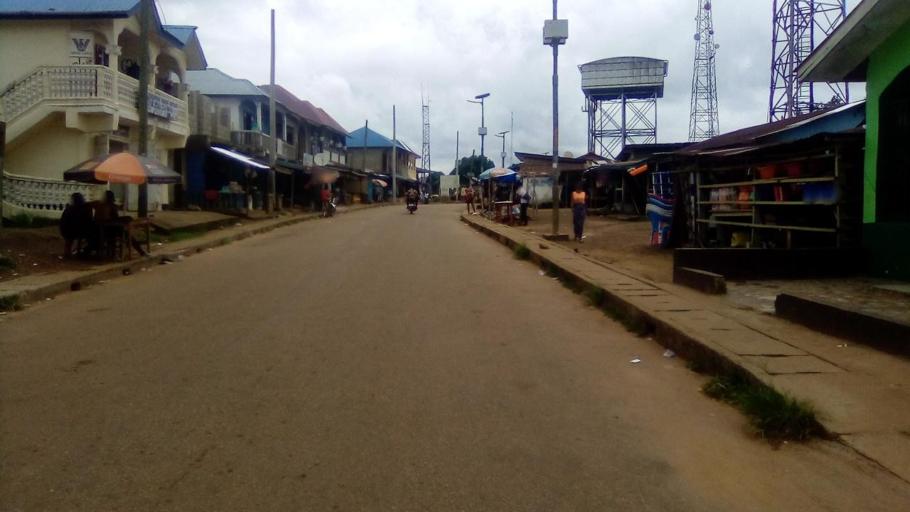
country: SL
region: Southern Province
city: Pujehun
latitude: 7.3570
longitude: -11.7209
